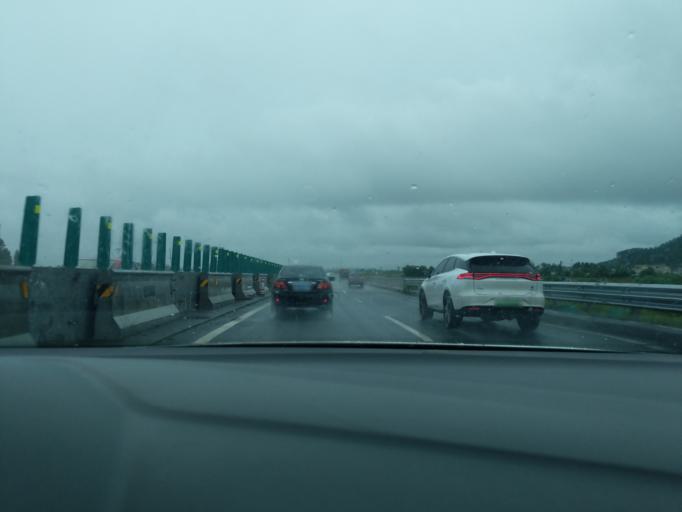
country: CN
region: Guangdong
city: Yueshan
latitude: 22.4641
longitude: 112.6956
